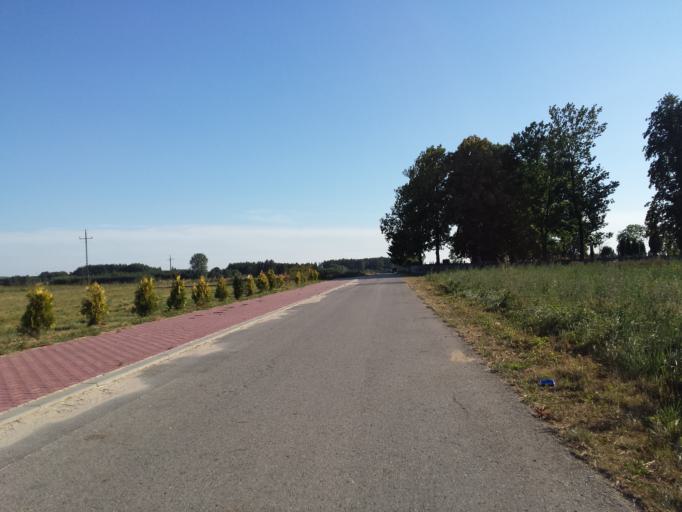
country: PL
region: Swietokrzyskie
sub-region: Powiat buski
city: Gnojno
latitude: 50.6557
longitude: 20.8404
